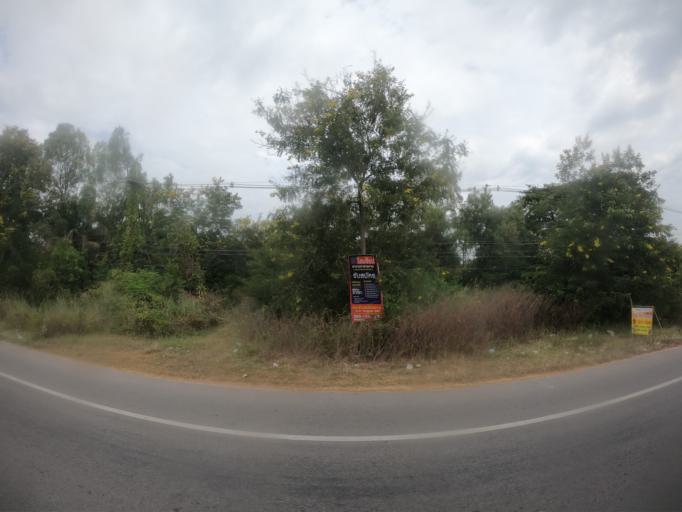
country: TH
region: Kalasin
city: Khong Chai
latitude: 16.1443
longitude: 103.4171
